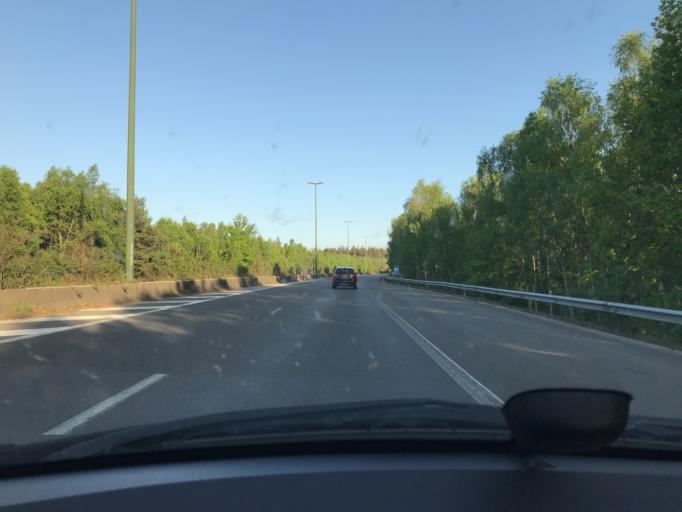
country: BE
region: Wallonia
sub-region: Province du Luxembourg
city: Tellin
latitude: 50.0615
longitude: 5.1994
